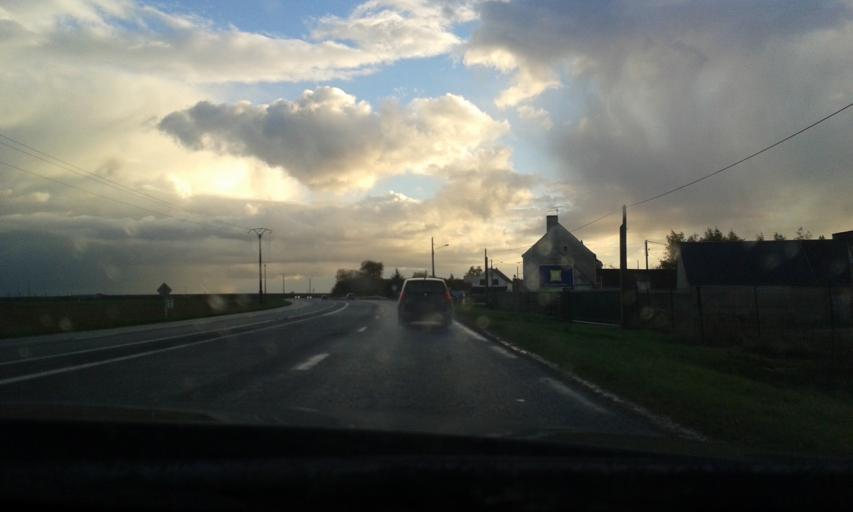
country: FR
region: Centre
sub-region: Departement du Loiret
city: Chevilly
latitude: 48.0538
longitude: 1.8755
